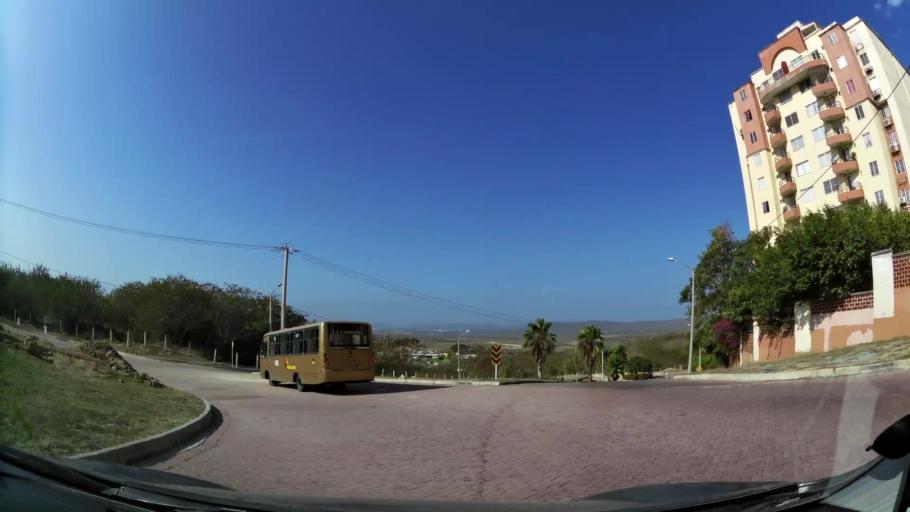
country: CO
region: Atlantico
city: Barranquilla
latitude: 10.9993
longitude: -74.8360
